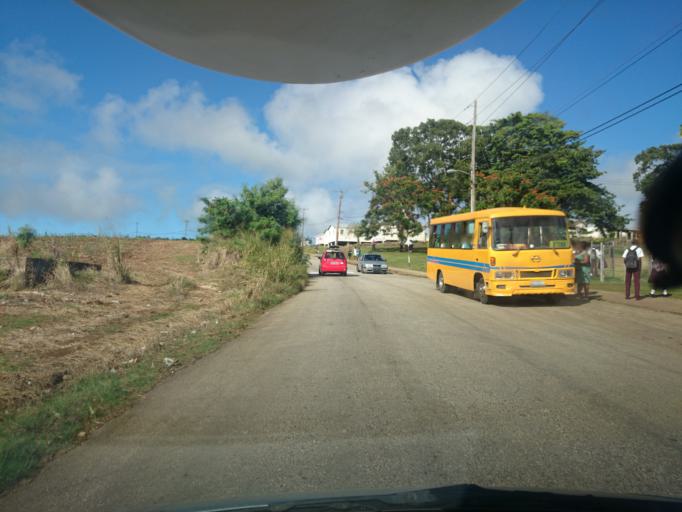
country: BB
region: Saint Thomas
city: Welchman Hall
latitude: 13.1874
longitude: -59.5441
